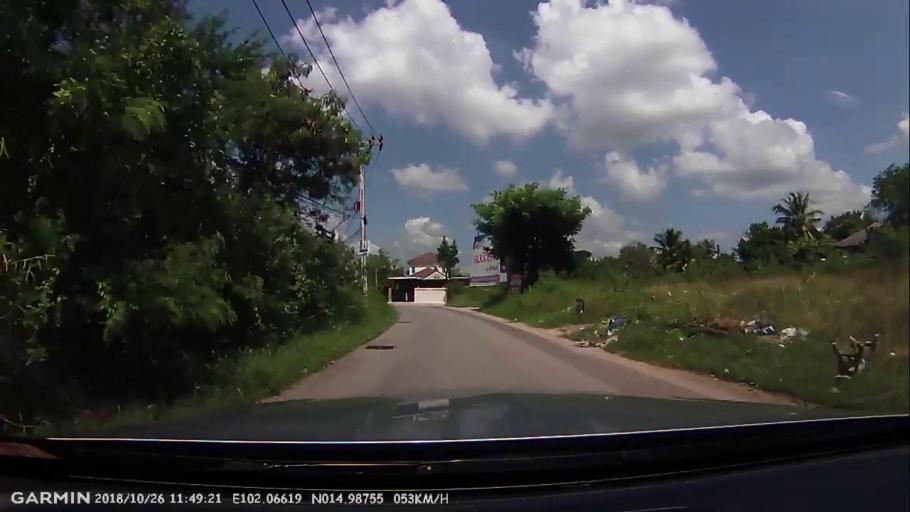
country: TH
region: Nakhon Ratchasima
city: Nakhon Ratchasima
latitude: 14.9876
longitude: 102.0662
